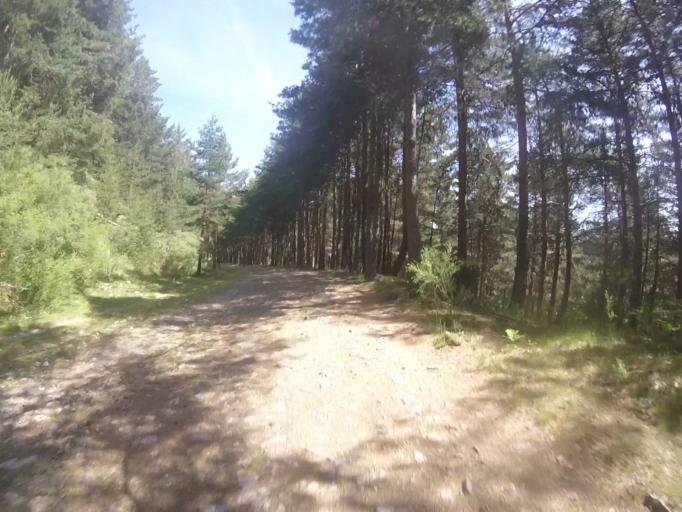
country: ES
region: Madrid
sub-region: Provincia de Madrid
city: Cercedilla
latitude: 40.8104
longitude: -4.0564
